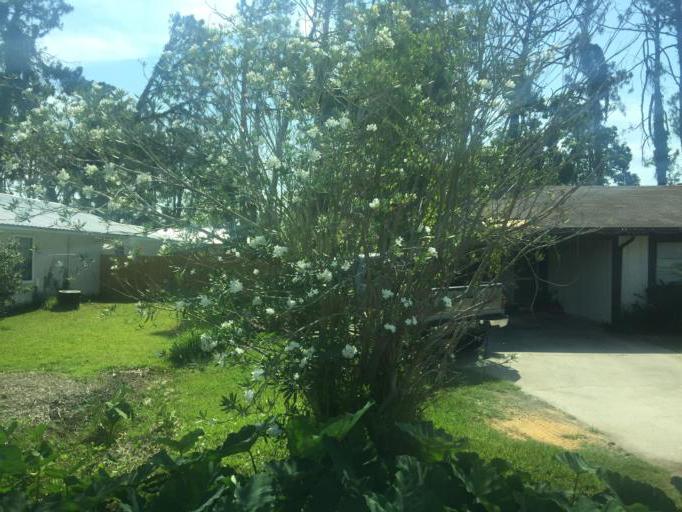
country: US
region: Florida
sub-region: Bay County
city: Lower Grand Lagoon
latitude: 30.1572
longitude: -85.7559
